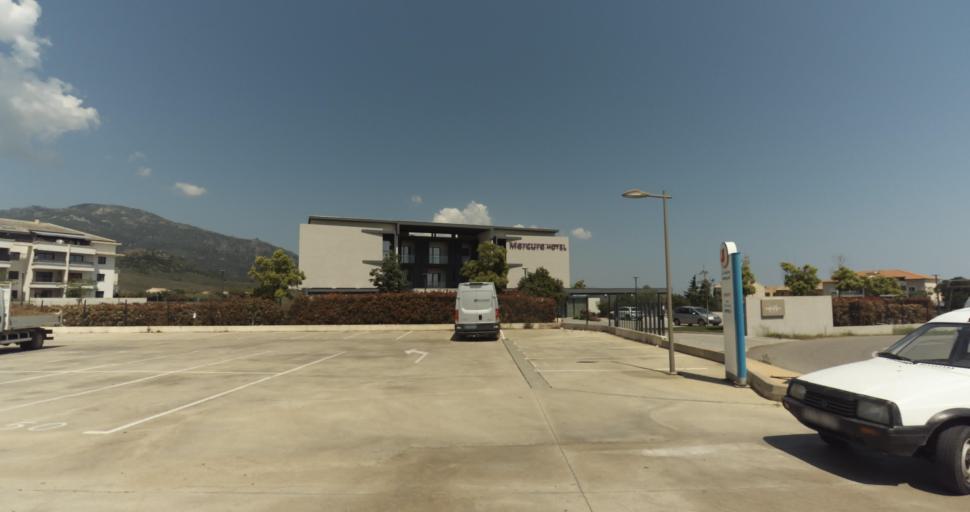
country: FR
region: Corsica
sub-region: Departement de la Haute-Corse
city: Biguglia
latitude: 42.5942
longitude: 9.4368
